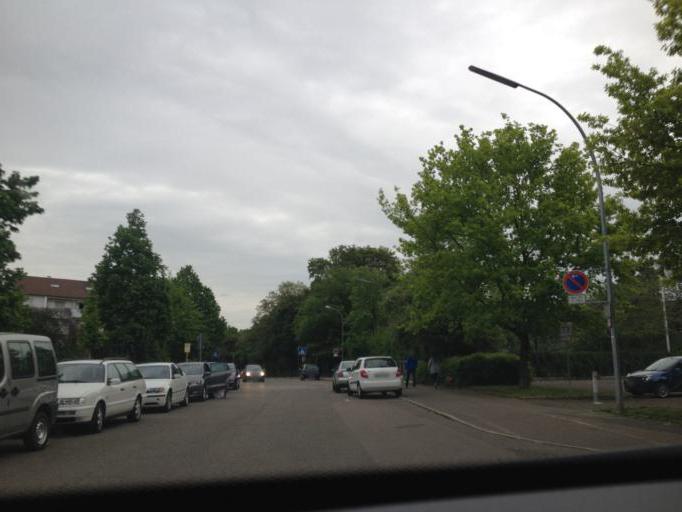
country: DE
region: Baden-Wuerttemberg
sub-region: Regierungsbezirk Stuttgart
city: Esslingen
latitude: 48.7308
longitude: 9.3407
